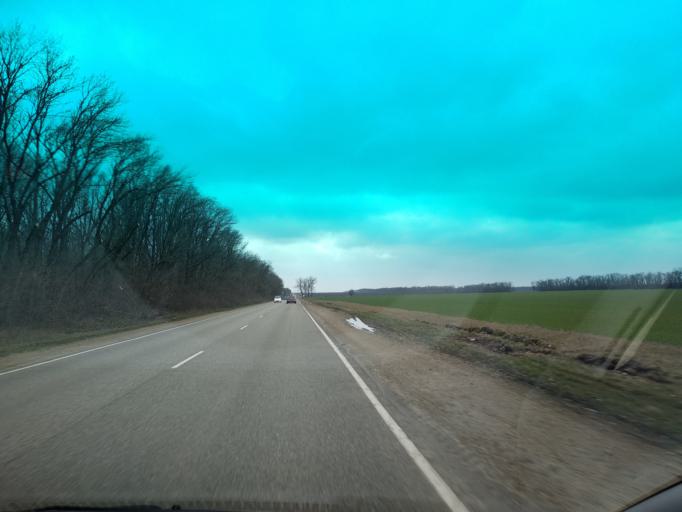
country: RU
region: Krasnodarskiy
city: Novorozhdestvenskaya
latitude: 45.7600
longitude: 39.9276
